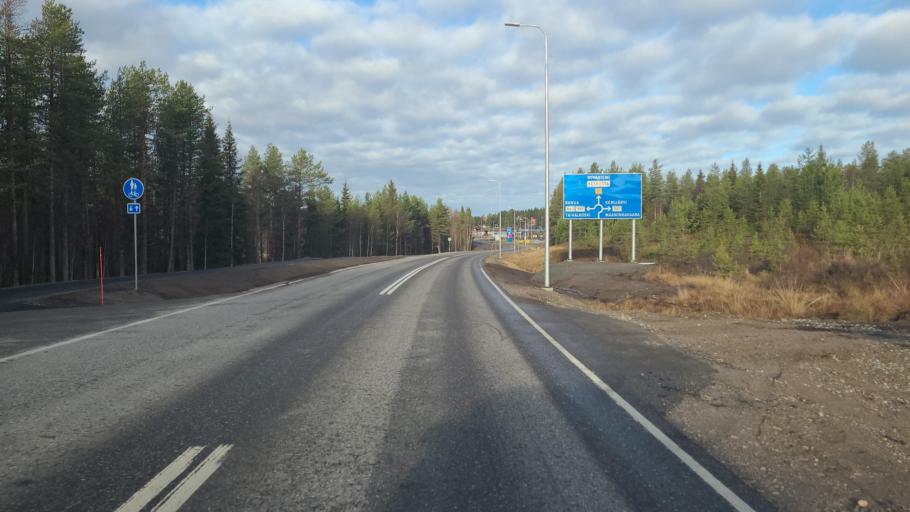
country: FI
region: Lapland
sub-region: Itae-Lappi
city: Posio
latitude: 66.1060
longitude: 28.1813
